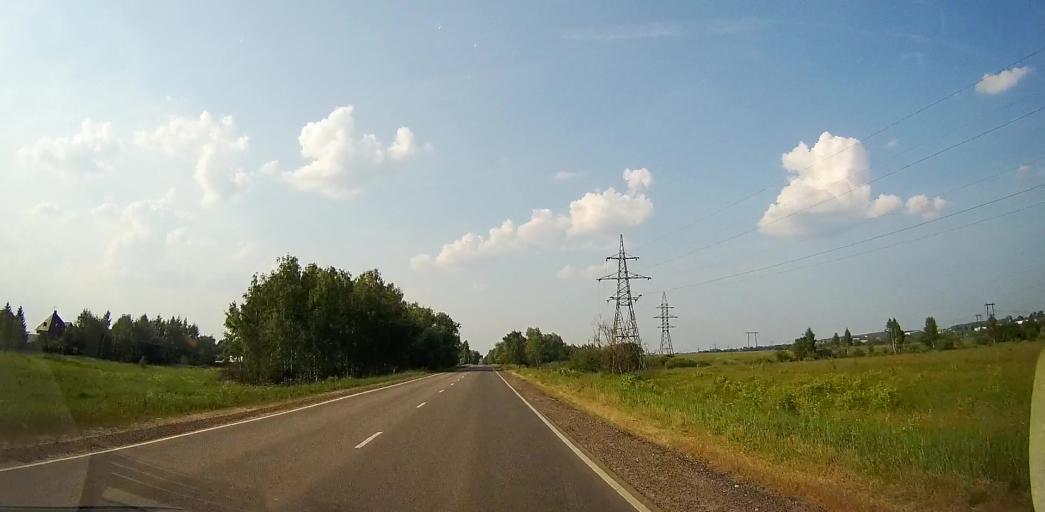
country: RU
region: Moskovskaya
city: Ostrovtsy
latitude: 55.5211
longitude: 38.0036
